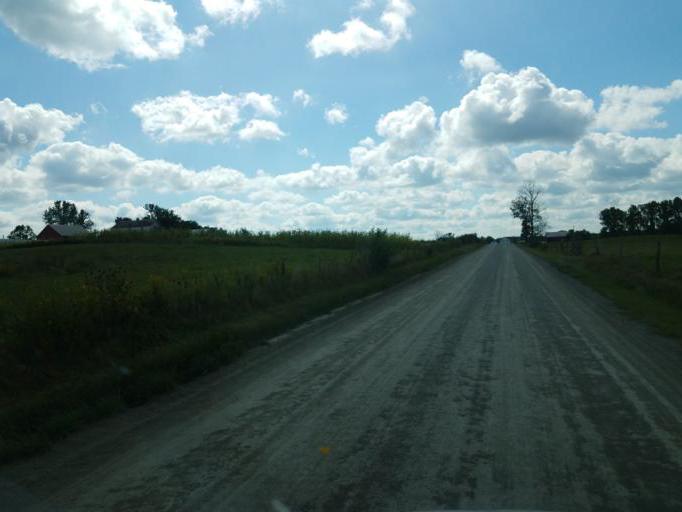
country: US
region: Ohio
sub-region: Wayne County
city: West Salem
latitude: 40.9950
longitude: -82.1465
